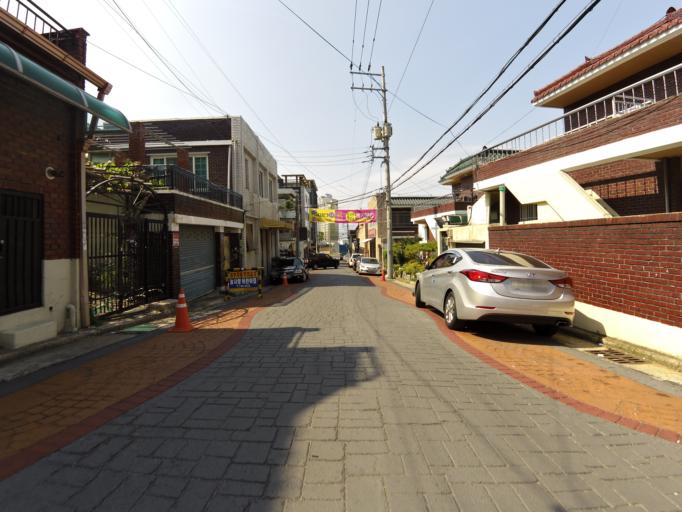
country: KR
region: Daegu
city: Daegu
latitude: 35.8650
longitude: 128.6425
